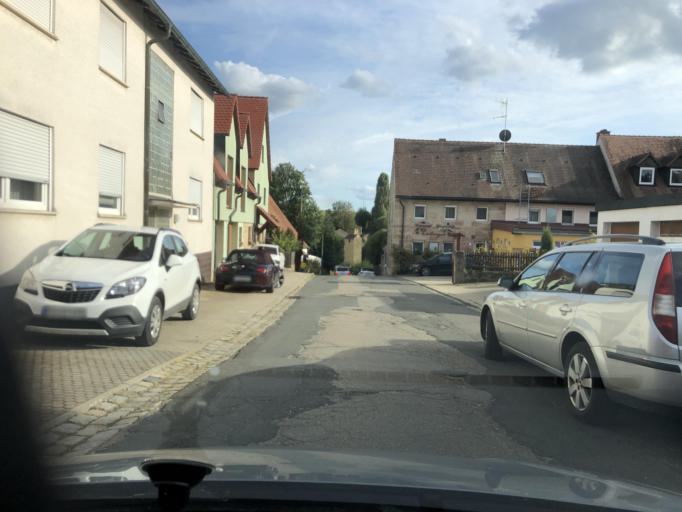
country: DE
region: Bavaria
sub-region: Regierungsbezirk Mittelfranken
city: Seukendorf
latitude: 49.4560
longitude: 10.8865
